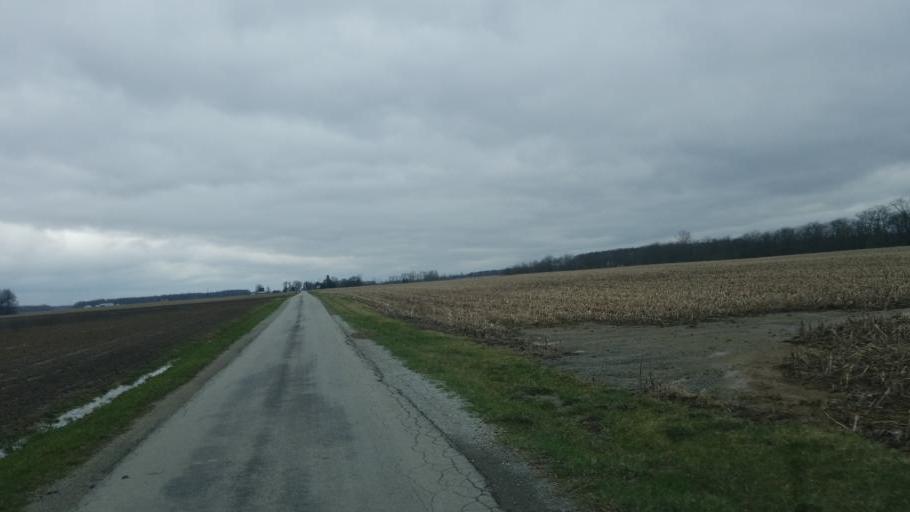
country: US
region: Ohio
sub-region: Hardin County
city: Forest
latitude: 40.7235
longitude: -83.4869
